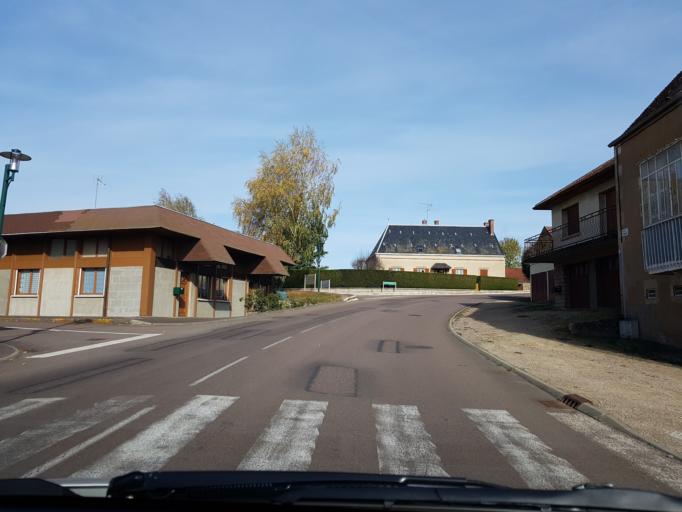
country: FR
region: Bourgogne
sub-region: Departement de la Cote-d'Or
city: Semur-en-Auxois
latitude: 47.4997
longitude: 4.1223
